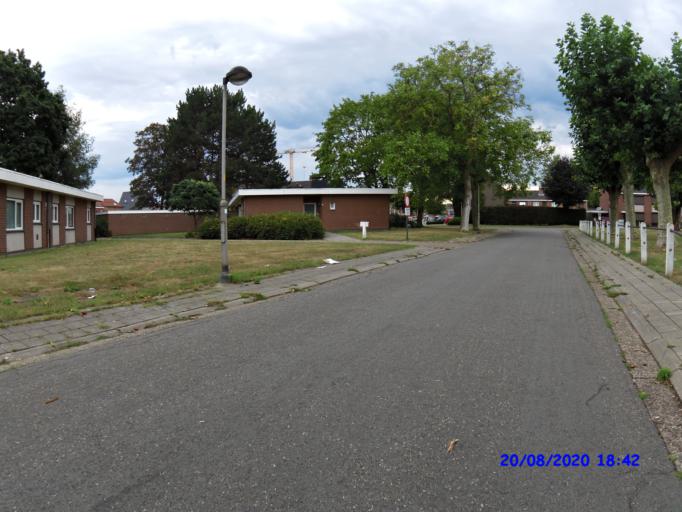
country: BE
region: Flanders
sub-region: Provincie Limburg
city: Sint-Truiden
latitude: 50.8270
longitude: 5.1777
